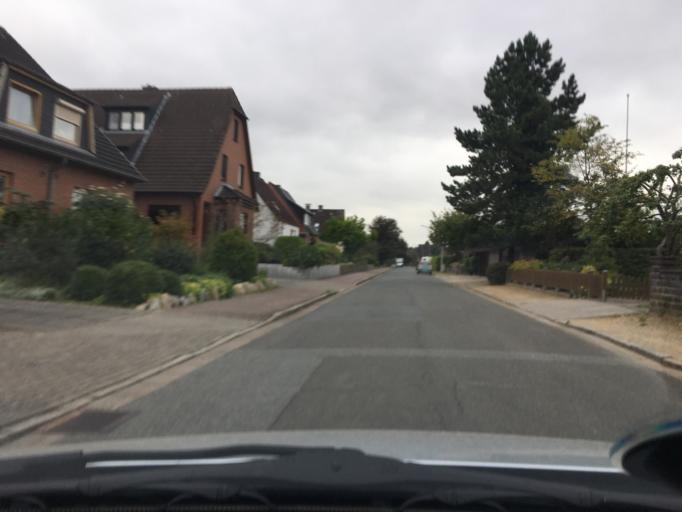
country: DE
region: Schleswig-Holstein
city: Melsdorf
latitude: 54.3140
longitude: 10.0257
